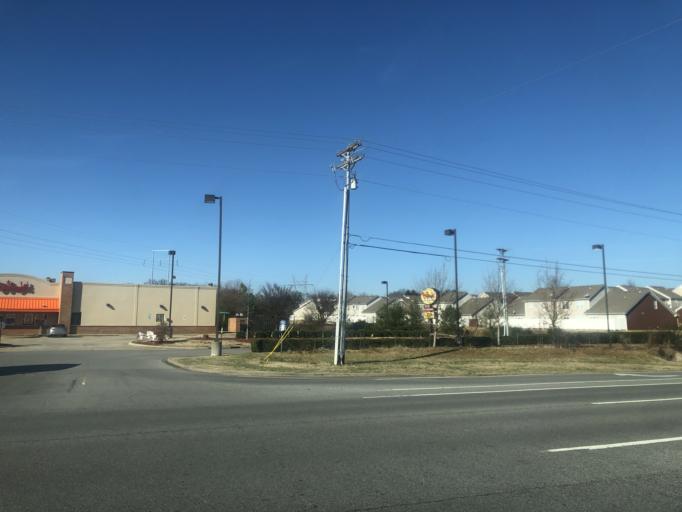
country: US
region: Tennessee
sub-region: Rutherford County
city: Smyrna
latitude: 35.9417
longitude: -86.5255
